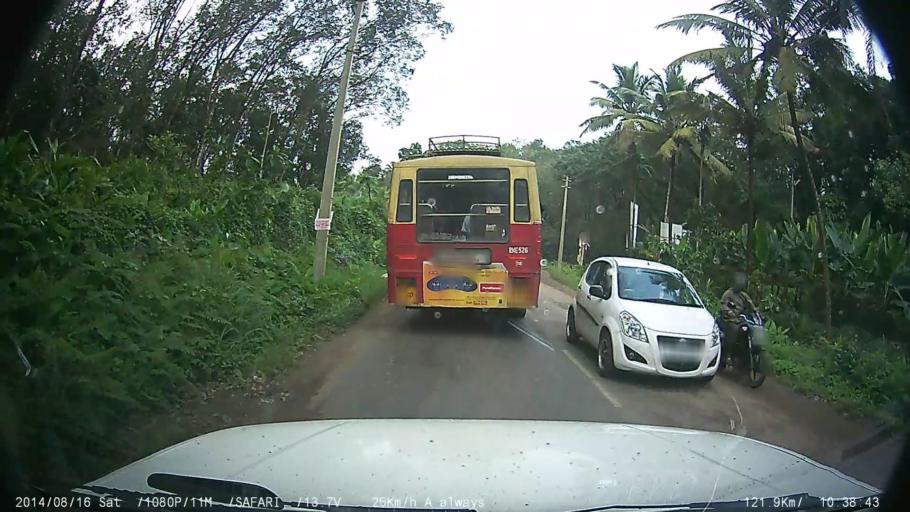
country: IN
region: Kerala
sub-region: Kottayam
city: Palackattumala
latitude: 9.7753
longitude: 76.5727
